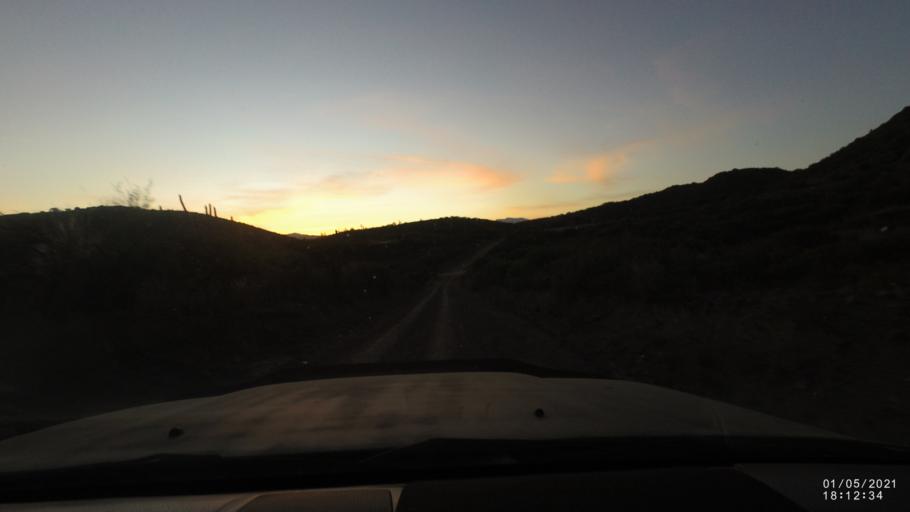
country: BO
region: Cochabamba
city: Capinota
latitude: -17.6776
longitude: -66.2021
